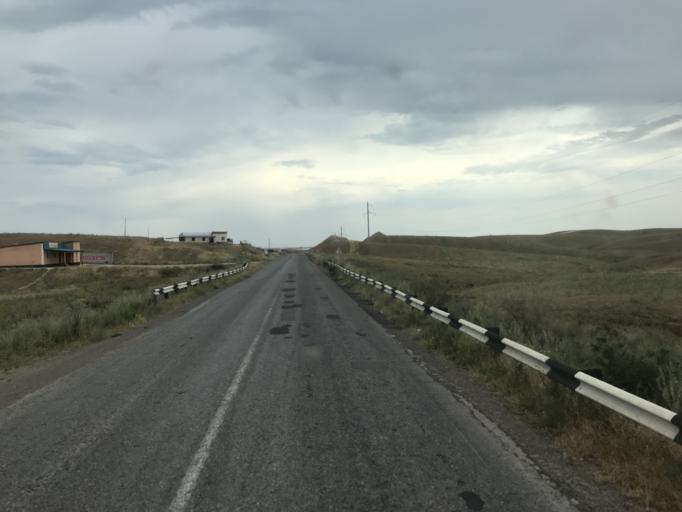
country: UZ
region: Toshkent
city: Chinoz
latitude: 41.0558
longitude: 68.5882
